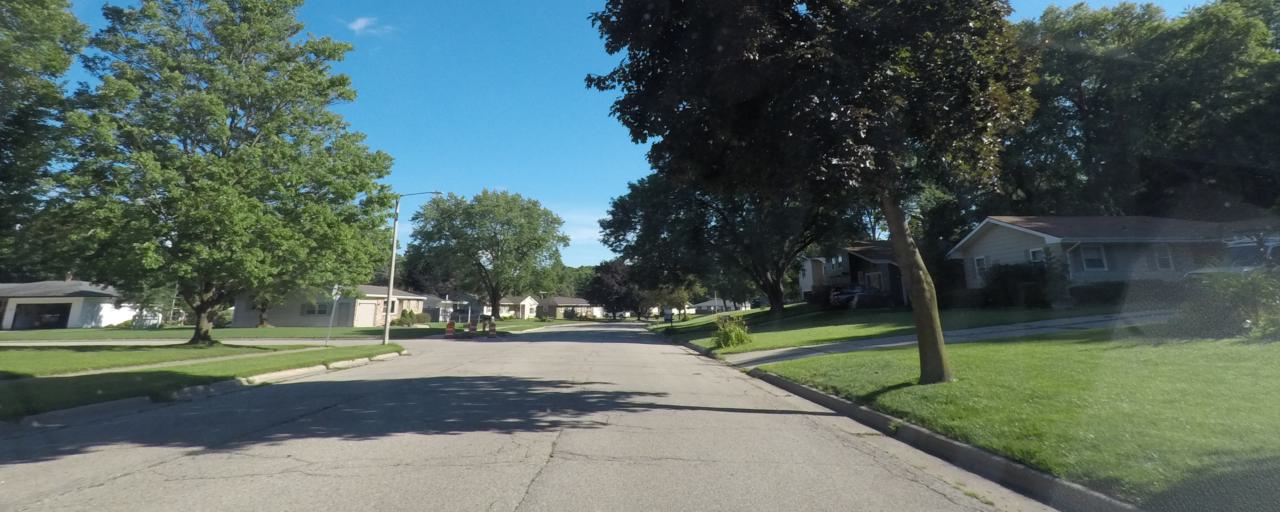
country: US
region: Wisconsin
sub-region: Rock County
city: Janesville
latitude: 42.6850
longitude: -88.9872
